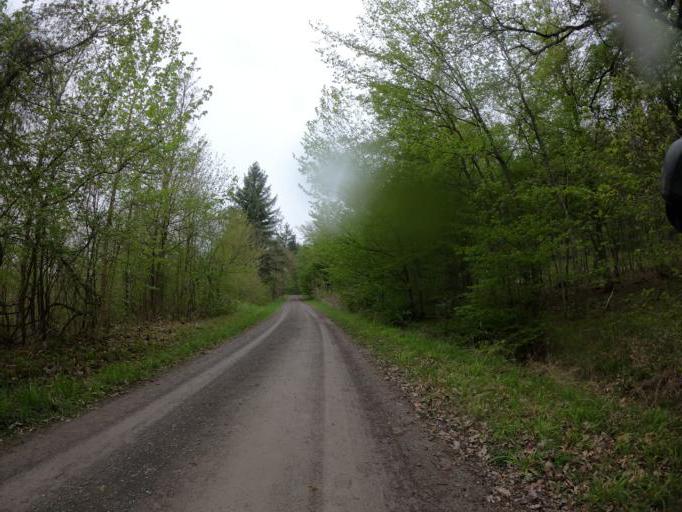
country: DE
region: Baden-Wuerttemberg
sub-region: Karlsruhe Region
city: Illingen
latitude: 48.9730
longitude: 8.8962
